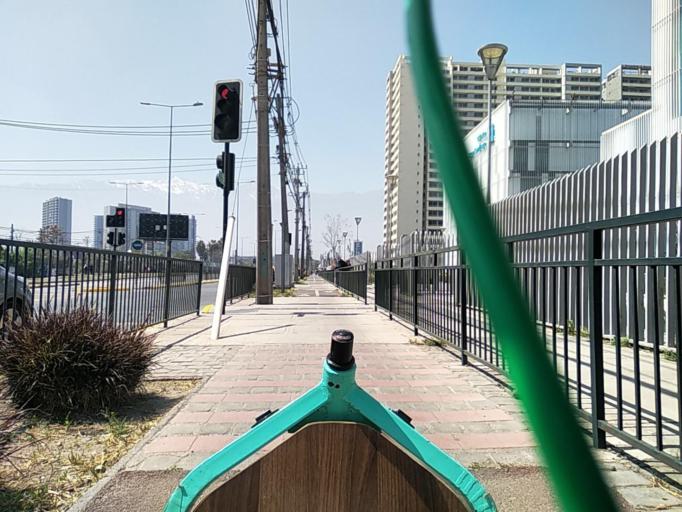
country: CL
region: Santiago Metropolitan
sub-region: Provincia de Santiago
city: Villa Presidente Frei, Nunoa, Santiago, Chile
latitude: -33.5095
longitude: -70.5982
